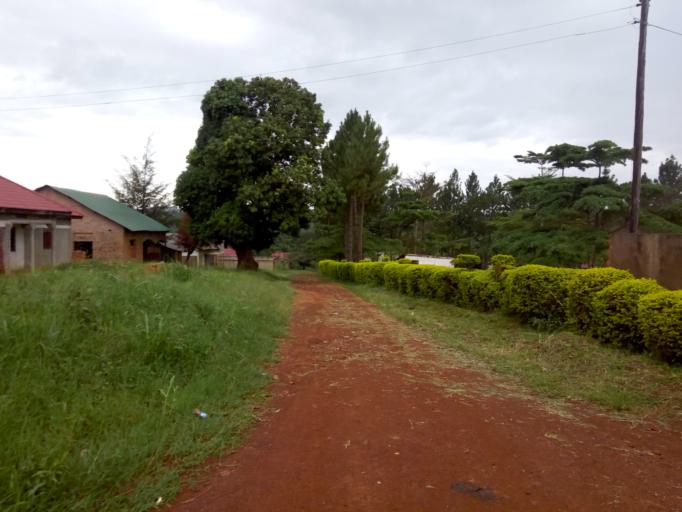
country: UG
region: Western Region
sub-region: Masindi District
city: Masindi
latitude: 1.6823
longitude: 31.7145
